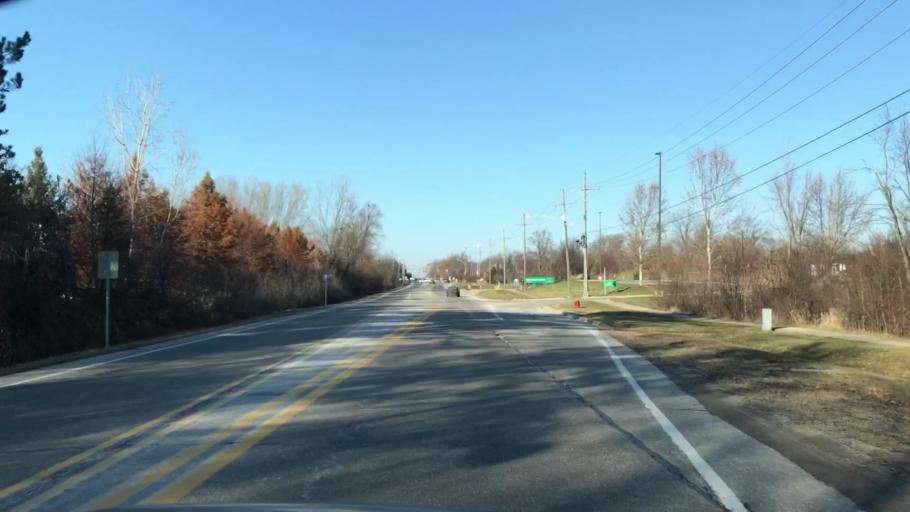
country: US
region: Michigan
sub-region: Oakland County
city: Novi
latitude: 42.4624
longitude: -83.4943
